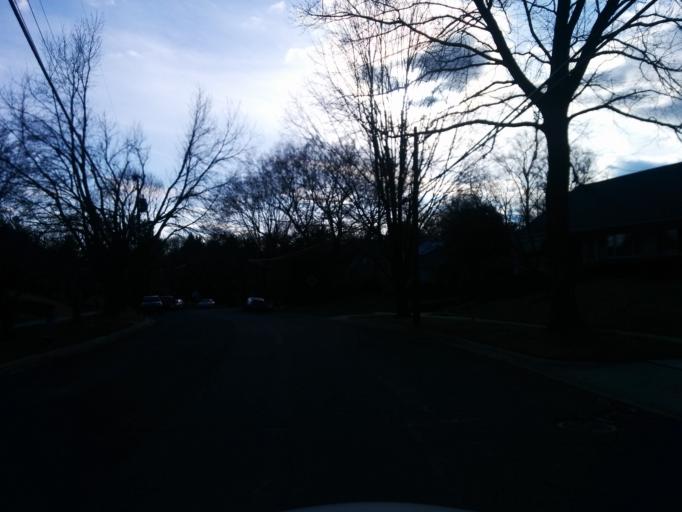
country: US
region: Maryland
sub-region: Montgomery County
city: Brookmont
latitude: 38.9554
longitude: -77.1182
